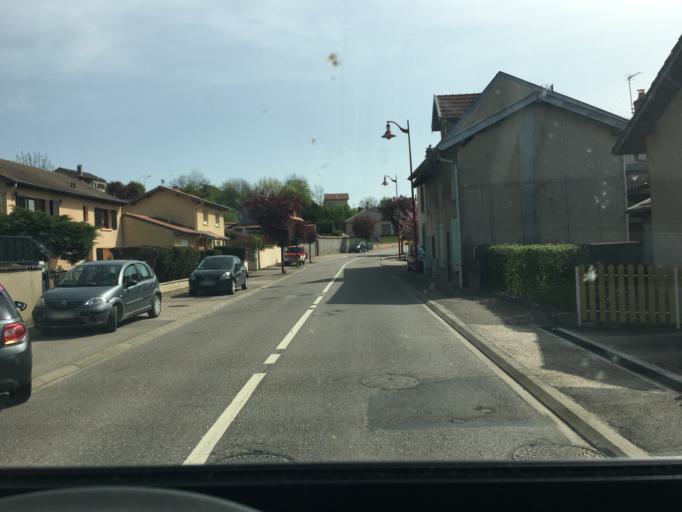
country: FR
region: Lorraine
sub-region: Departement de Meurthe-et-Moselle
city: Messein
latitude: 48.6100
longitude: 6.1463
